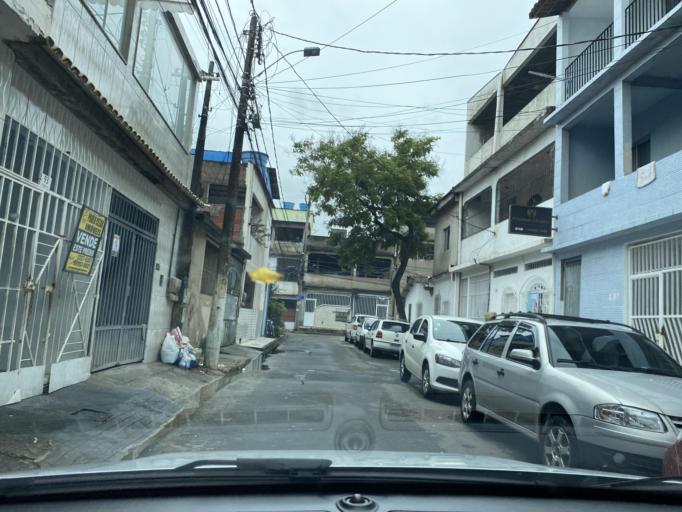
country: BR
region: Espirito Santo
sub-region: Vila Velha
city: Vila Velha
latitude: -20.2555
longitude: -40.2925
